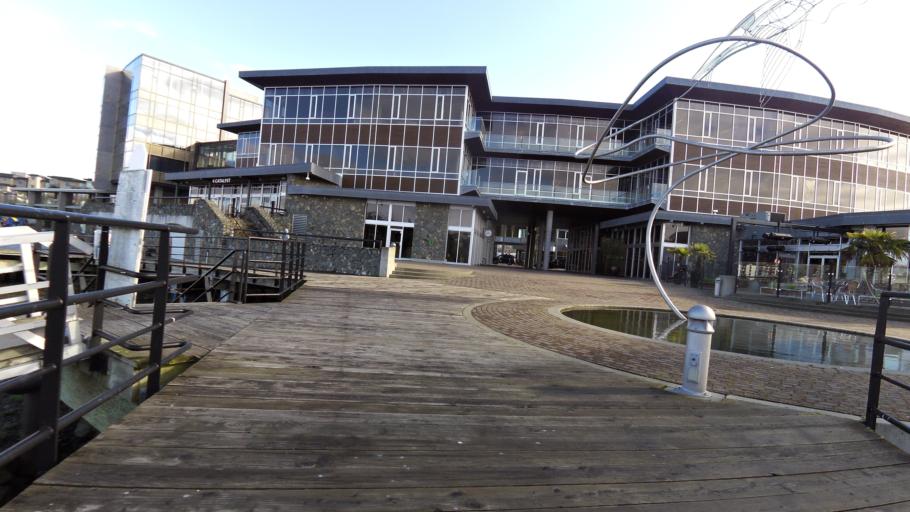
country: CA
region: British Columbia
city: Victoria
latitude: 48.4387
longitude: -123.3795
